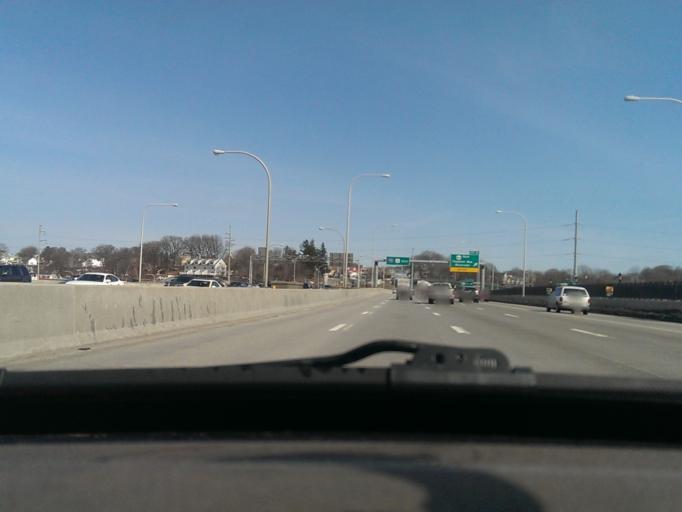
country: US
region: Rhode Island
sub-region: Providence County
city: East Providence
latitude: 41.8191
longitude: -71.3861
